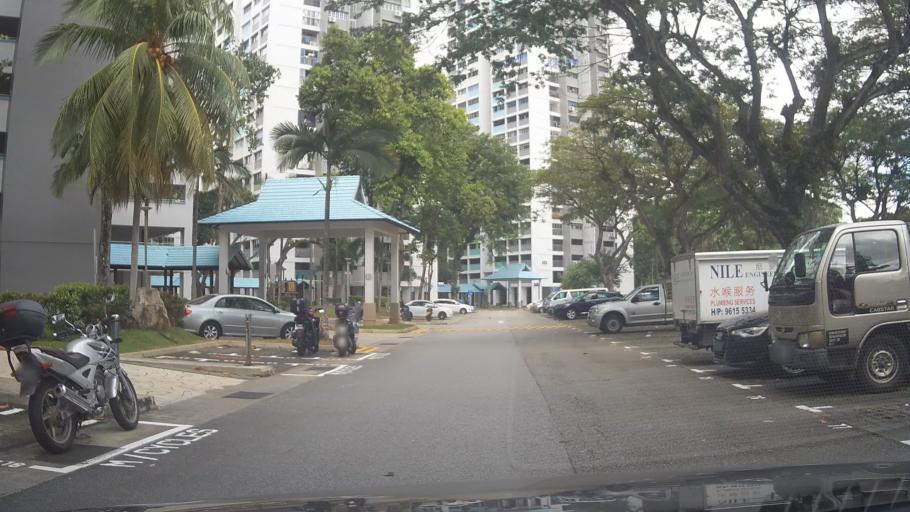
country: MY
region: Johor
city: Johor Bahru
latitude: 1.4465
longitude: 103.7738
